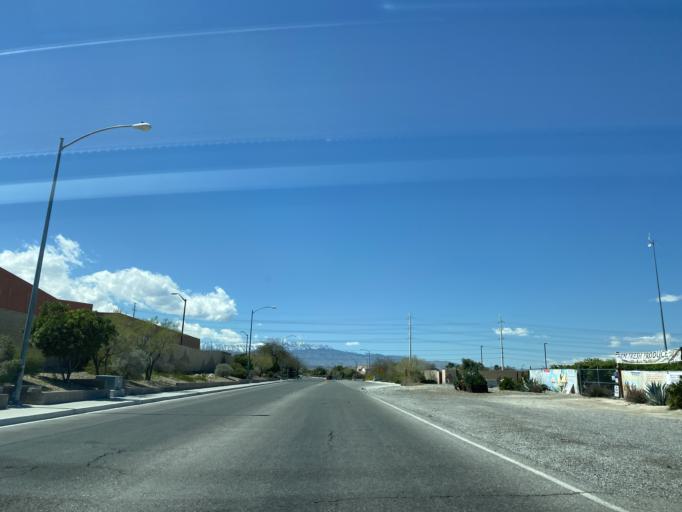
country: US
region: Nevada
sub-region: Clark County
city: North Las Vegas
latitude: 36.3134
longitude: -115.2043
